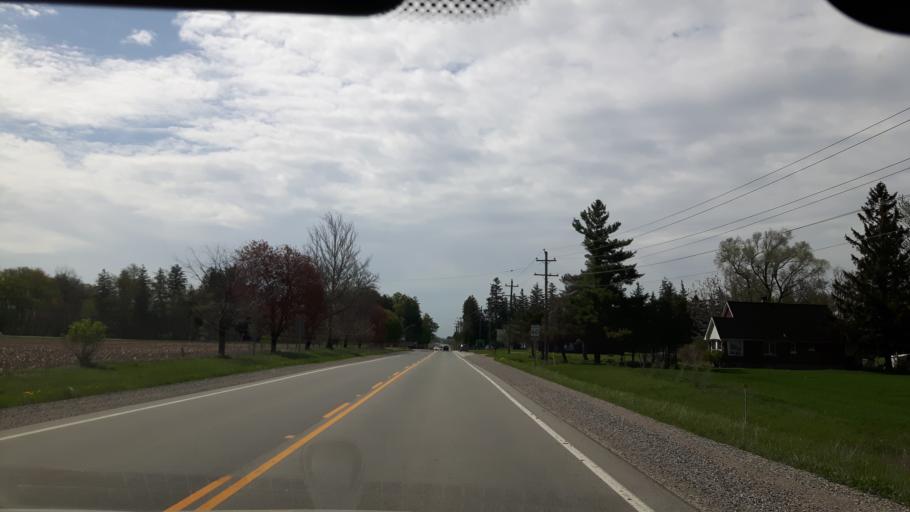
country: CA
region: Ontario
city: London
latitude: 43.1235
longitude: -81.3328
